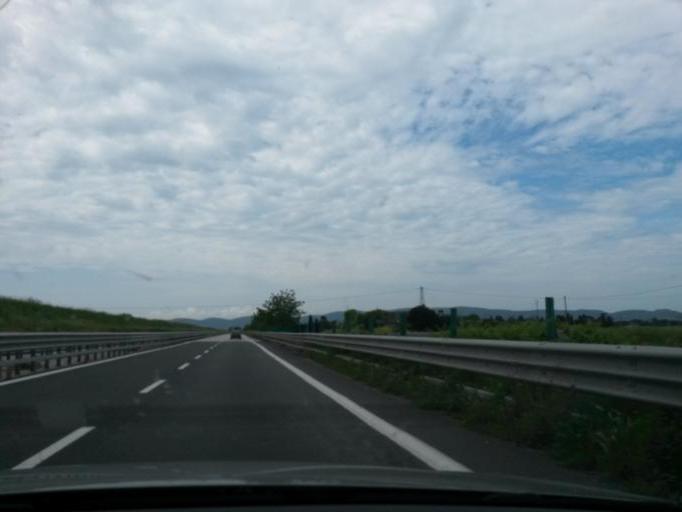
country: IT
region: Tuscany
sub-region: Provincia di Livorno
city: Venturina
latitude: 42.9972
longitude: 10.5794
